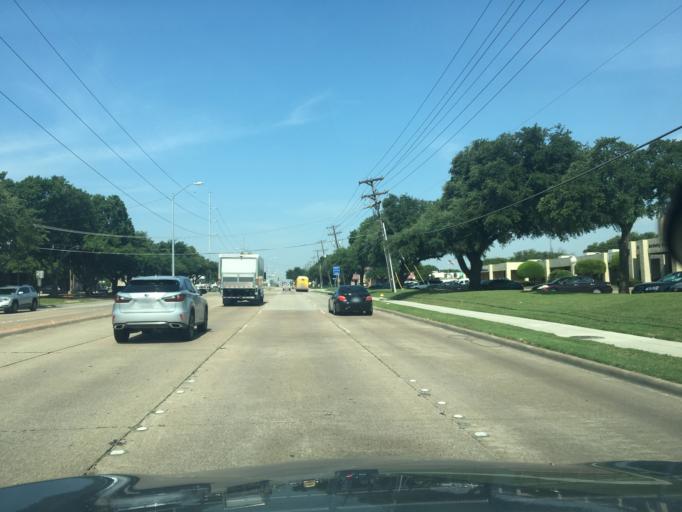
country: US
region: Texas
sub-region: Dallas County
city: Richardson
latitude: 32.9608
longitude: -96.7099
